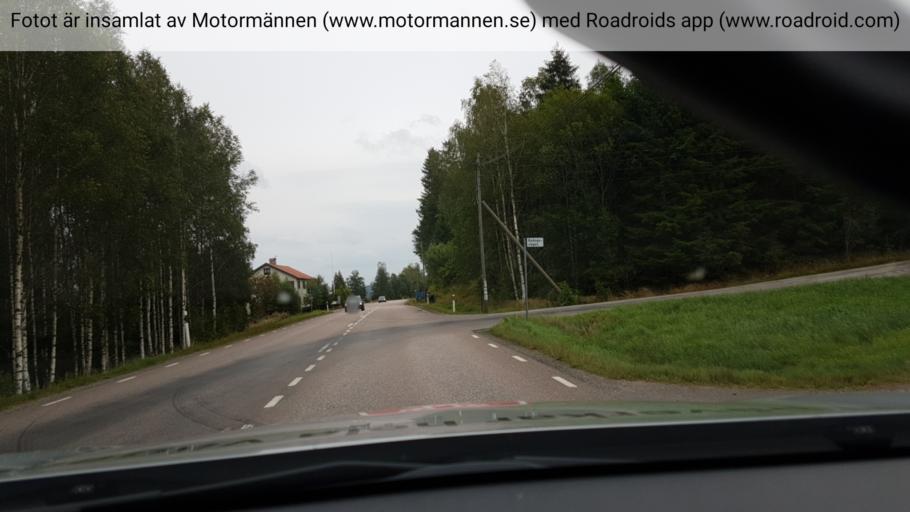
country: SE
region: Vaestra Goetaland
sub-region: Harryda Kommun
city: Landvetter
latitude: 57.6062
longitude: 12.2535
